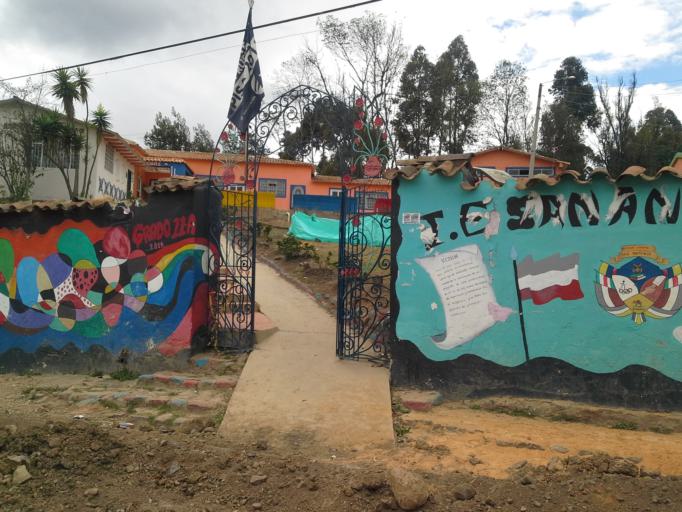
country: CO
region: Boyaca
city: Raquira
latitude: 5.5409
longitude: -73.6329
